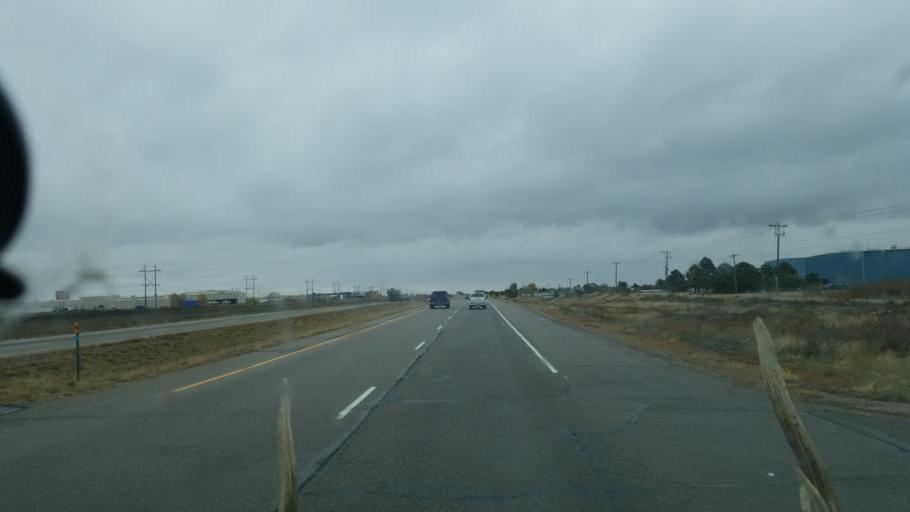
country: US
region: Colorado
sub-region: Pueblo County
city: Pueblo
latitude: 38.2743
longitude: -104.5312
